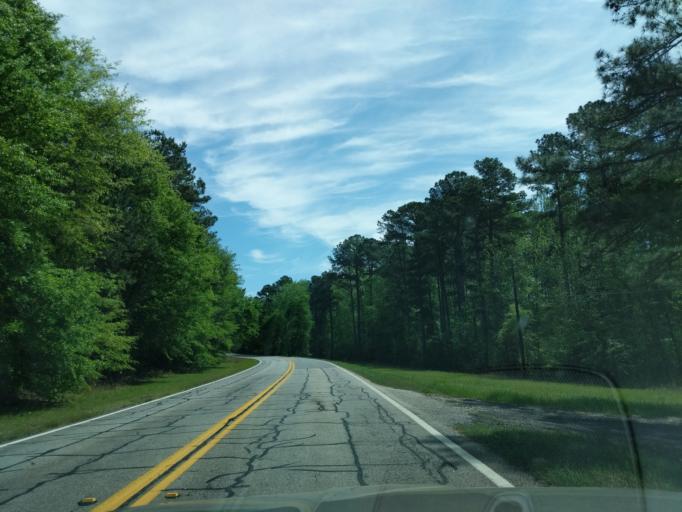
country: US
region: Georgia
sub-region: Columbia County
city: Appling
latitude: 33.6118
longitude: -82.3053
